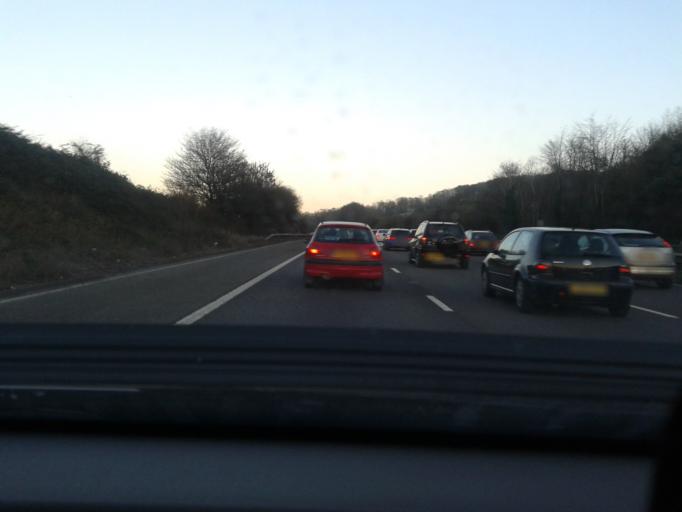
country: GB
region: England
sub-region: North Somerset
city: Portishead
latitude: 51.4587
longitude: -2.7628
